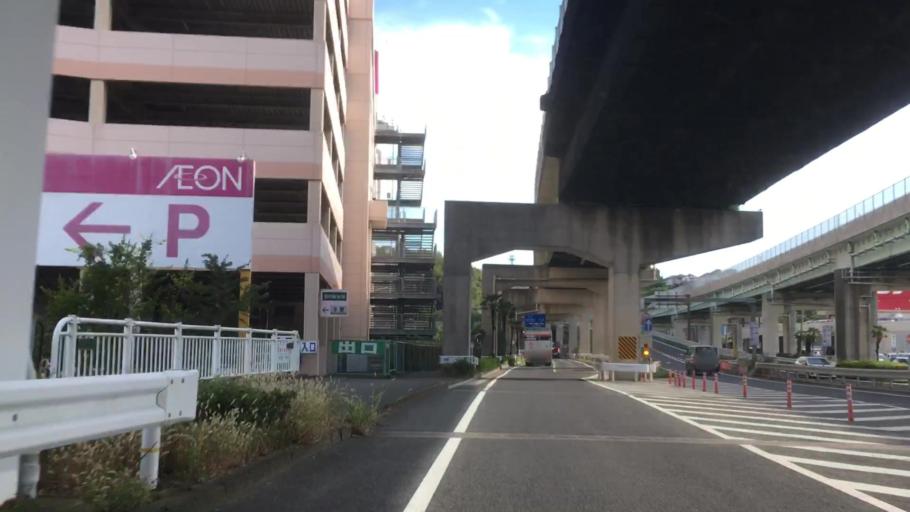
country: JP
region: Nagasaki
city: Sasebo
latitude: 33.1477
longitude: 129.7798
